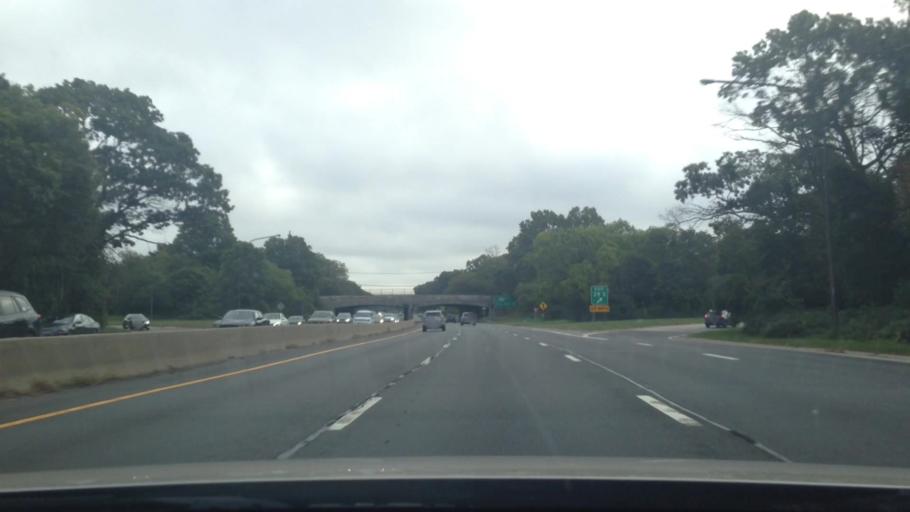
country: US
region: New York
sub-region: Suffolk County
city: North Babylon
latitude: 40.7317
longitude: -73.3238
